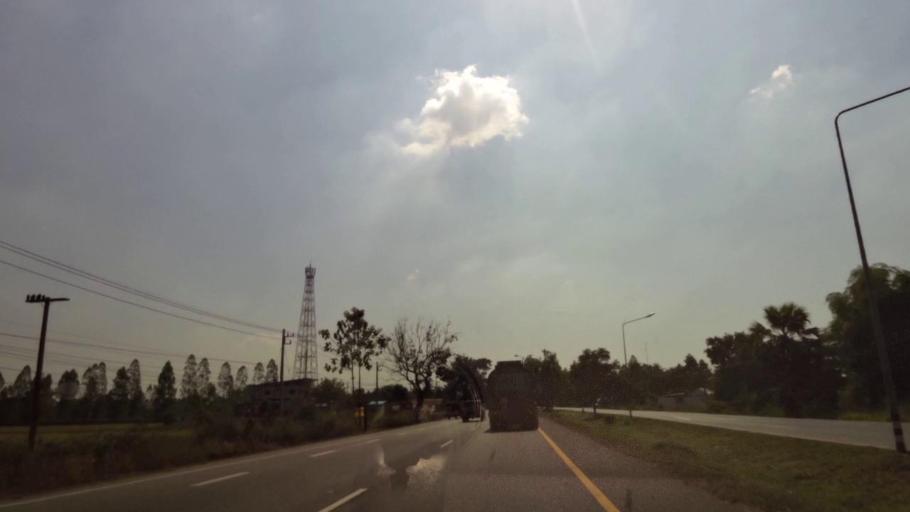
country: TH
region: Phichit
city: Bueng Na Rang
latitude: 16.1605
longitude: 100.1258
